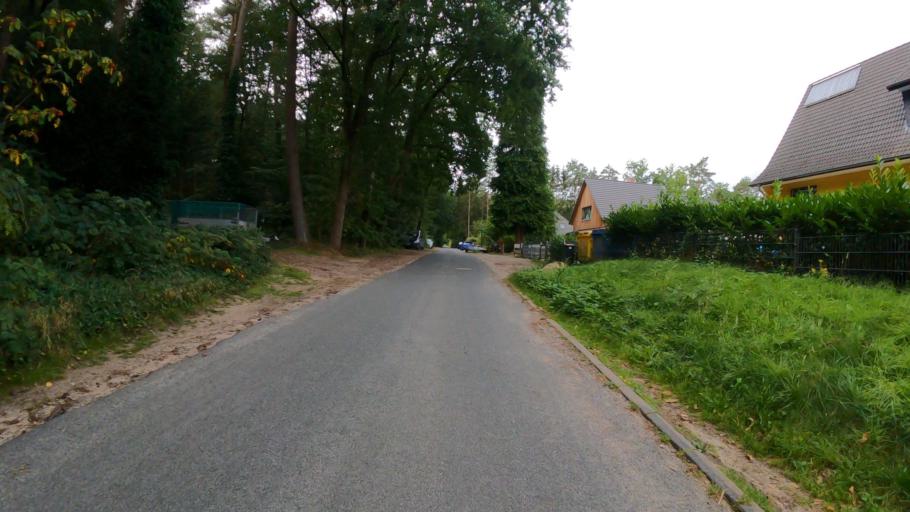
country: DE
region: Lower Saxony
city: Appel
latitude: 53.4060
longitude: 9.7864
